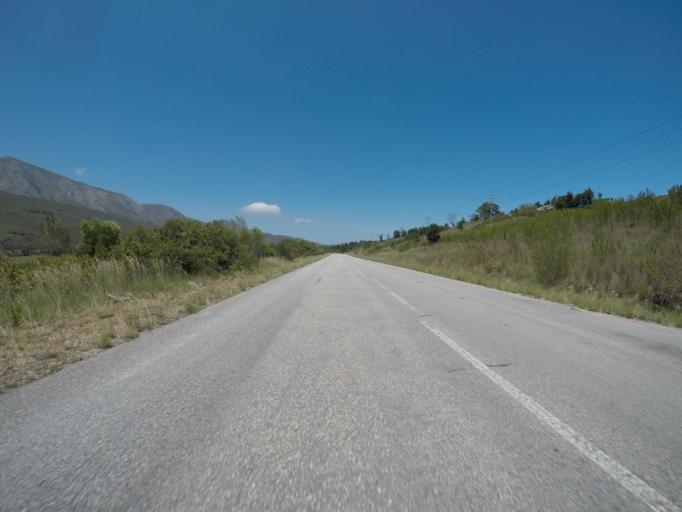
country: ZA
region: Eastern Cape
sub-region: Cacadu District Municipality
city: Kareedouw
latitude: -33.9134
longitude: 24.1776
